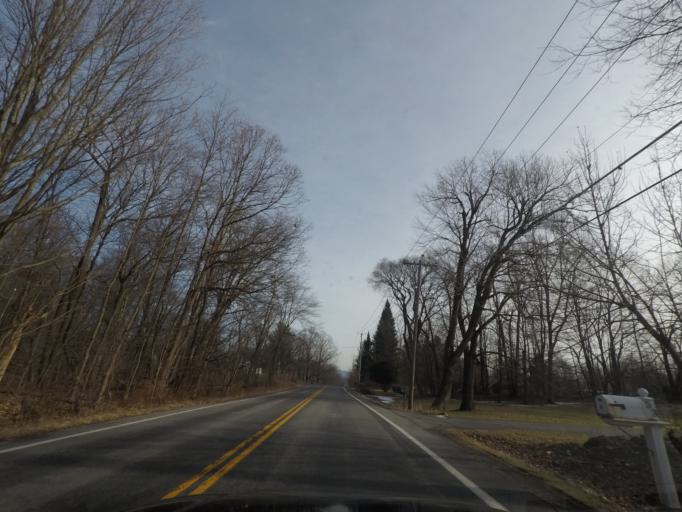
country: US
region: New York
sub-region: Saratoga County
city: Stillwater
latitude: 42.9851
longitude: -73.6776
